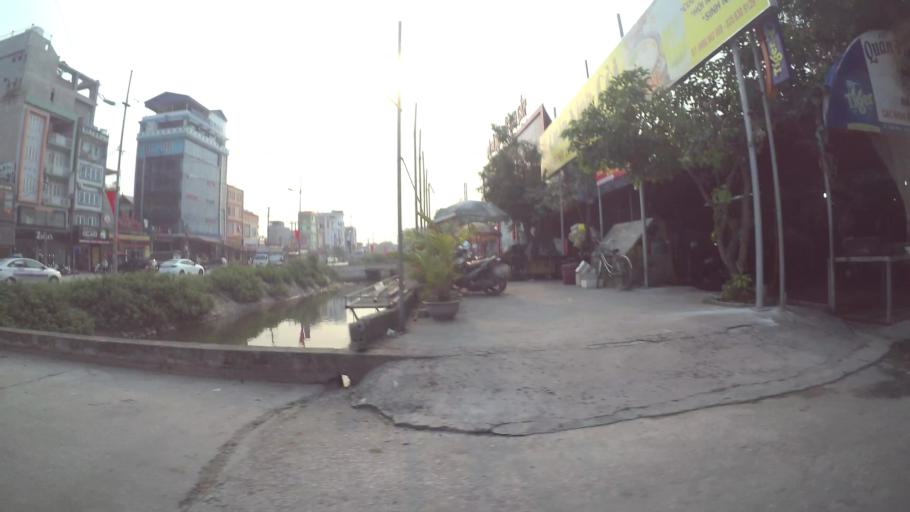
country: VN
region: Ha Noi
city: Thuong Tin
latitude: 20.8719
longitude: 105.8696
